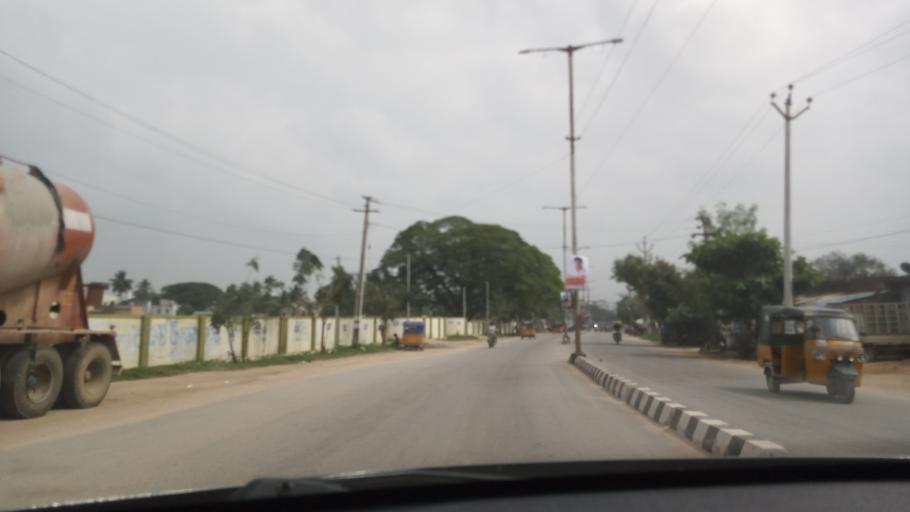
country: IN
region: Andhra Pradesh
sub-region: Chittoor
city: Madanapalle
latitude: 13.5559
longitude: 78.4941
